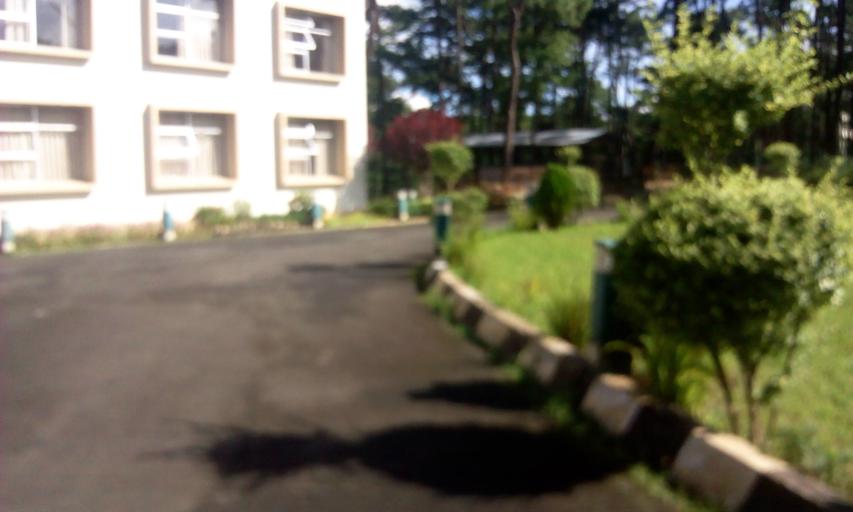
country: IN
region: Meghalaya
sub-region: East Khasi Hills
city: Shillong
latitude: 25.6107
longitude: 91.8937
